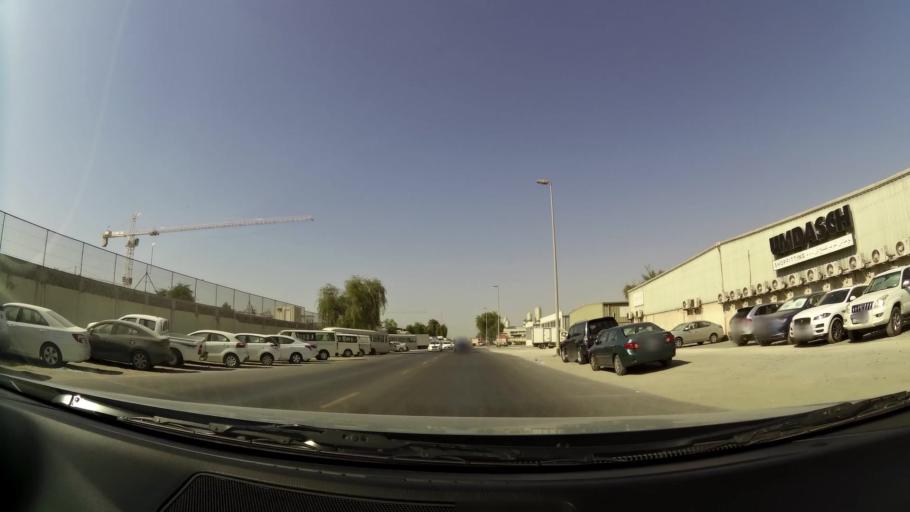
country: AE
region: Dubai
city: Dubai
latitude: 25.1250
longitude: 55.2227
